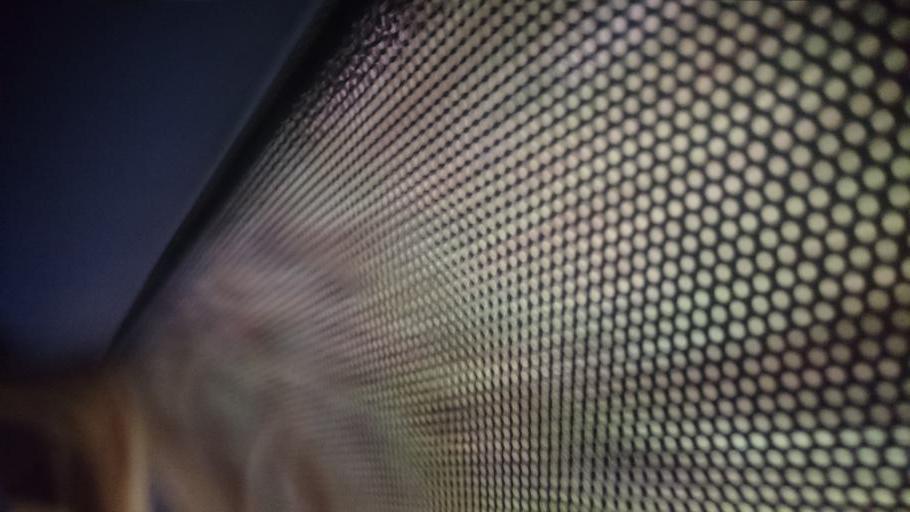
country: ES
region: Asturias
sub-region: Province of Asturias
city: Amieva
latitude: 43.3038
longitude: -5.0499
